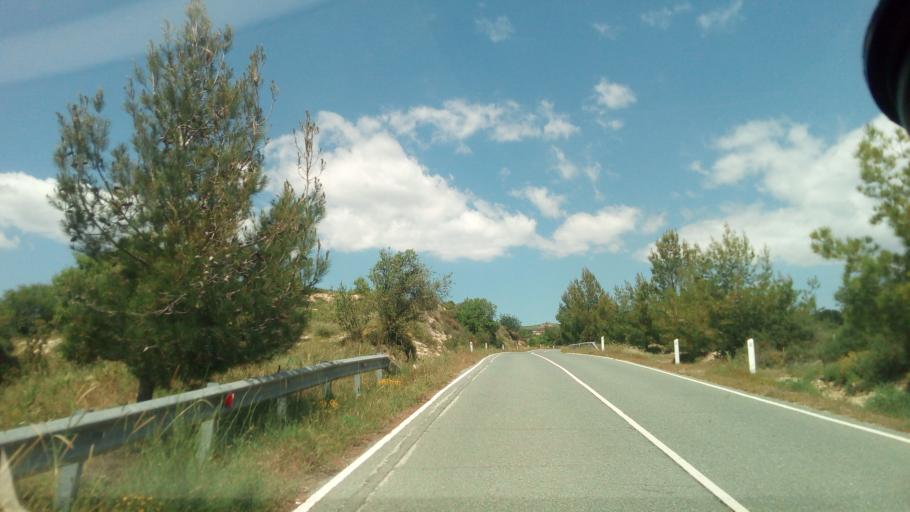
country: CY
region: Limassol
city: Pachna
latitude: 34.8258
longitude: 32.7693
